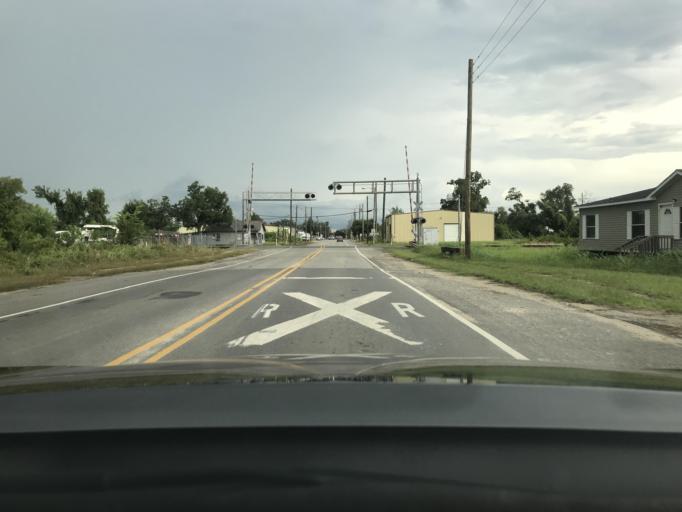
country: US
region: Louisiana
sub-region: Calcasieu Parish
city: Westlake
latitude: 30.2376
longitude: -93.2505
